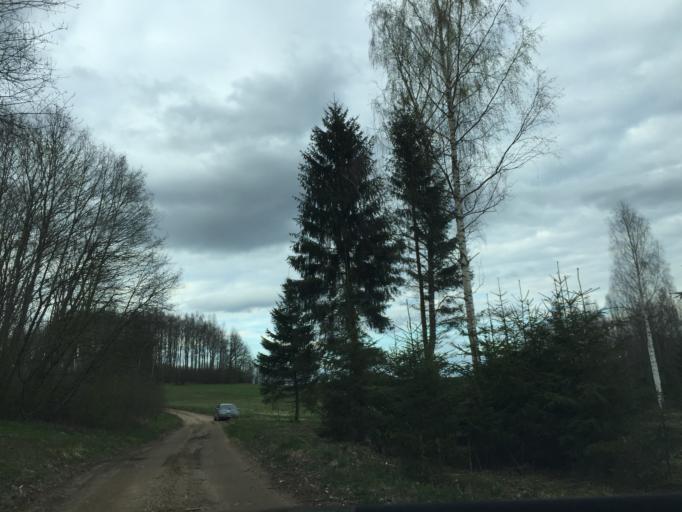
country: LV
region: Aluksnes Rajons
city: Aluksne
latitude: 57.3845
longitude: 26.9881
